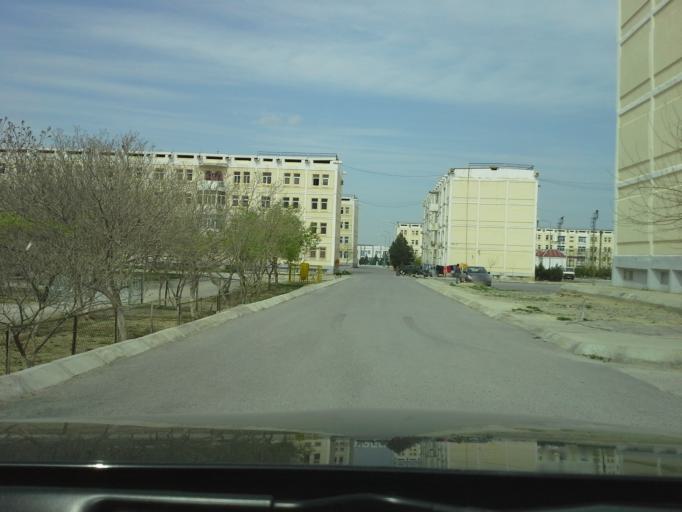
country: TM
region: Ahal
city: Abadan
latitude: 38.0541
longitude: 58.1430
